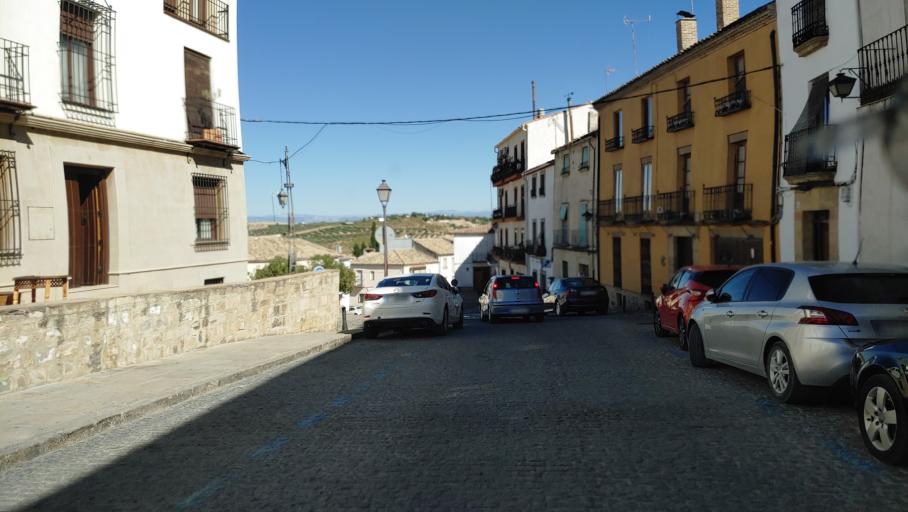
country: ES
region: Andalusia
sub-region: Provincia de Jaen
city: Ubeda
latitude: 38.0116
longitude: -3.3675
